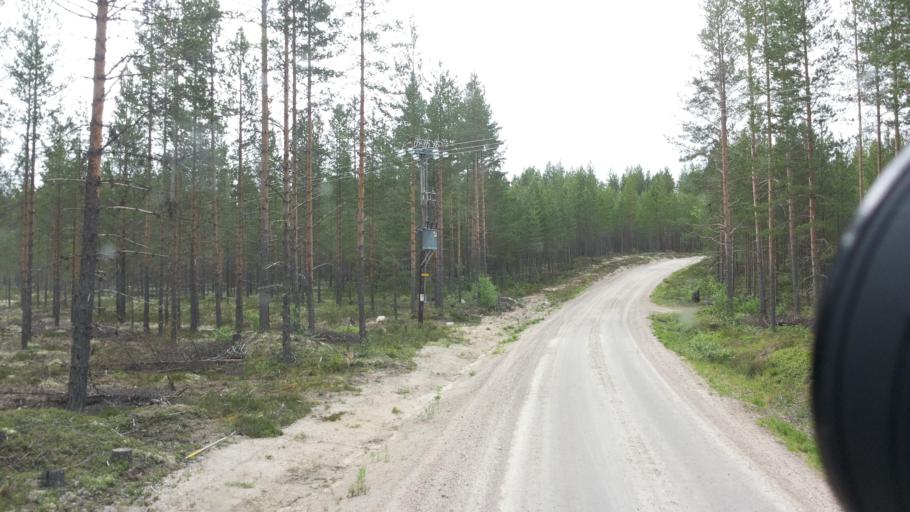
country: SE
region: Gaevleborg
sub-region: Ovanakers Kommun
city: Edsbyn
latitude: 61.5210
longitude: 15.3561
